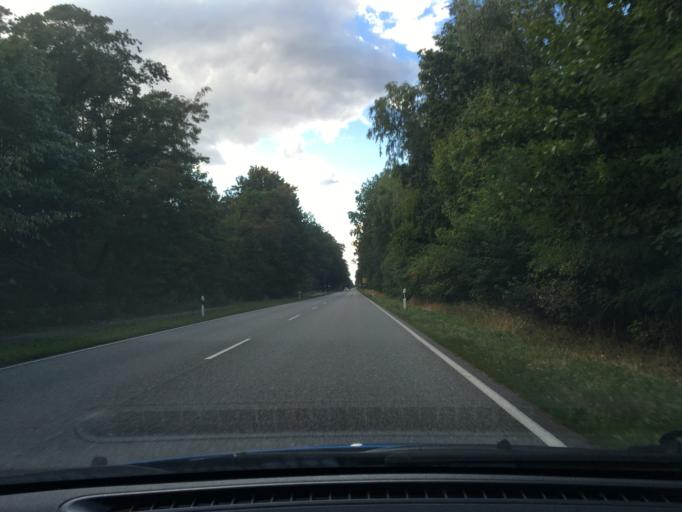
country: DE
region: Mecklenburg-Vorpommern
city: Ludwigslust
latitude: 53.3074
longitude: 11.5198
